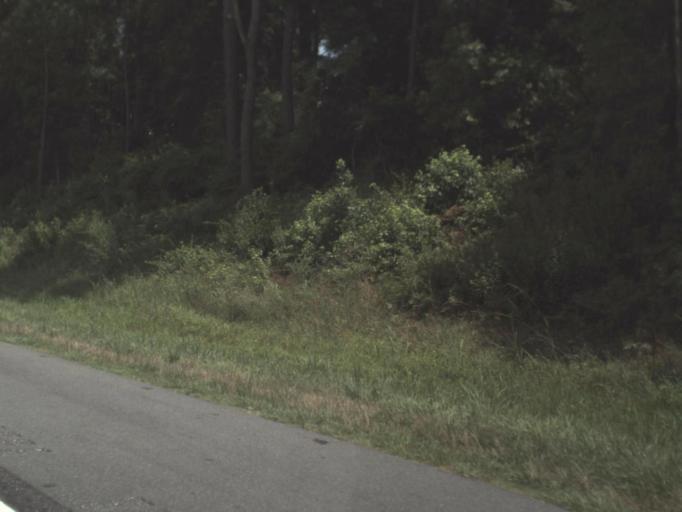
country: US
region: Florida
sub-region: Hamilton County
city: Jasper
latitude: 30.4935
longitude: -83.0311
